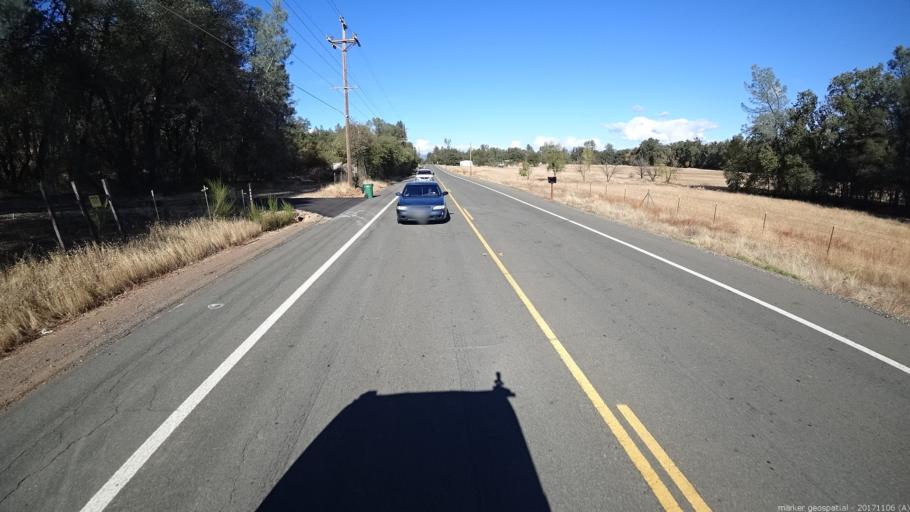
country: US
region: California
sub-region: Shasta County
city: Palo Cedro
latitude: 40.5909
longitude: -122.3084
